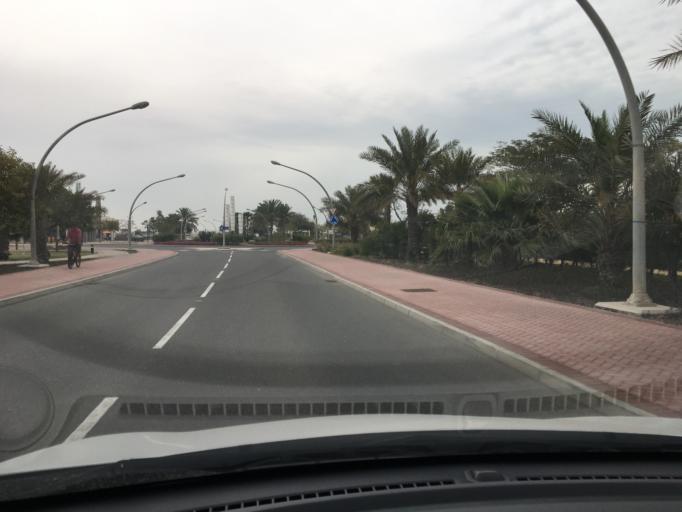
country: BH
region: Central Governorate
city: Dar Kulayb
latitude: 25.8384
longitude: 50.6152
